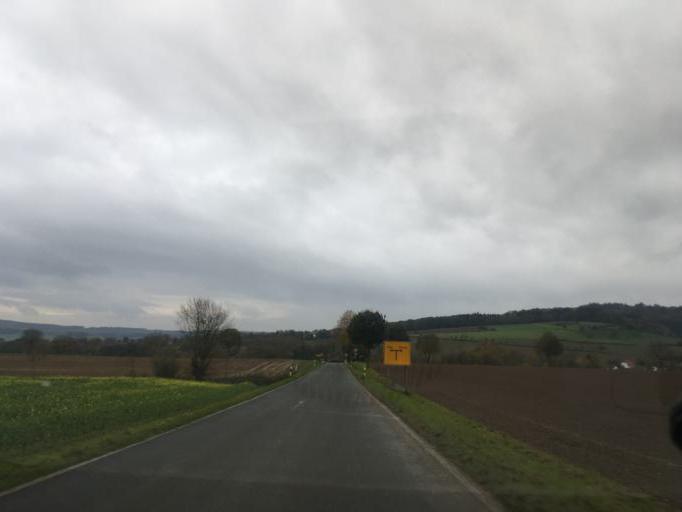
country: DE
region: Lower Saxony
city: Uslar
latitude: 51.6740
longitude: 9.6412
